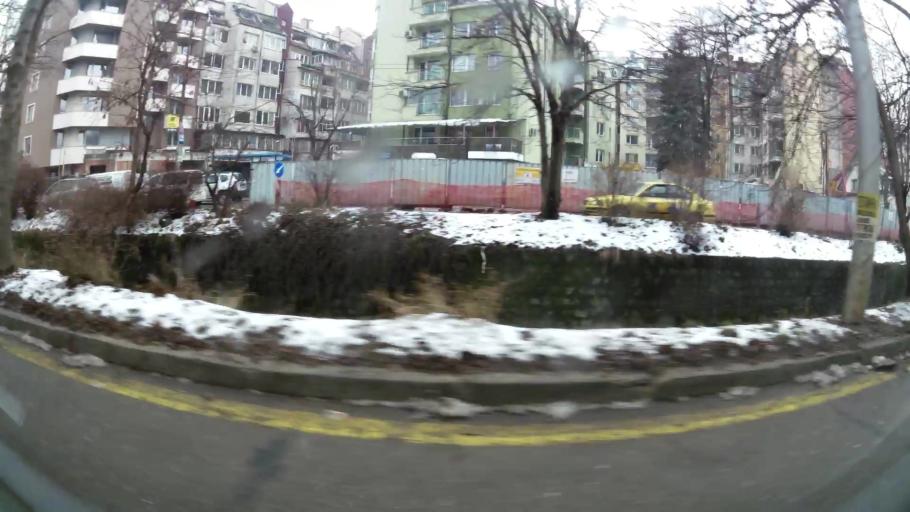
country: BG
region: Sofia-Capital
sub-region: Stolichna Obshtina
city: Sofia
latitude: 42.6788
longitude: 23.2921
